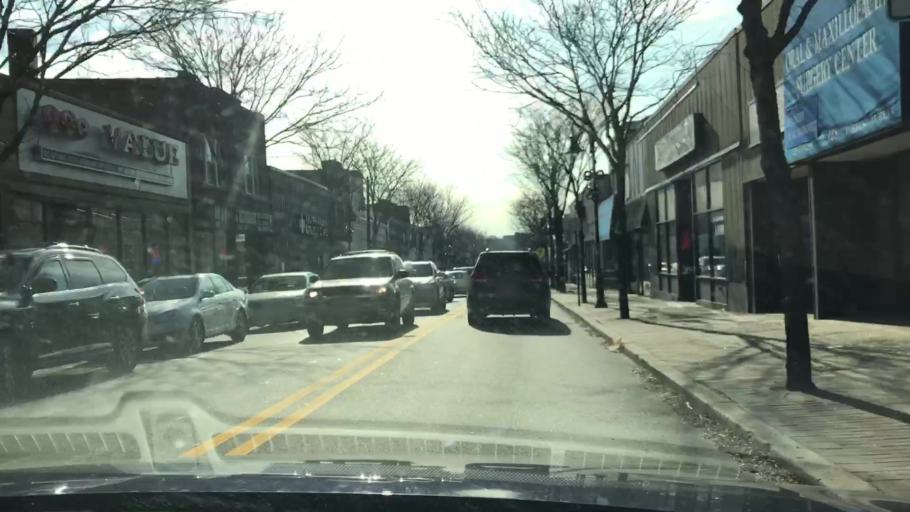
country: US
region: New Jersey
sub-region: Bergen County
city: Bergenfield
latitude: 40.9275
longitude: -73.9962
